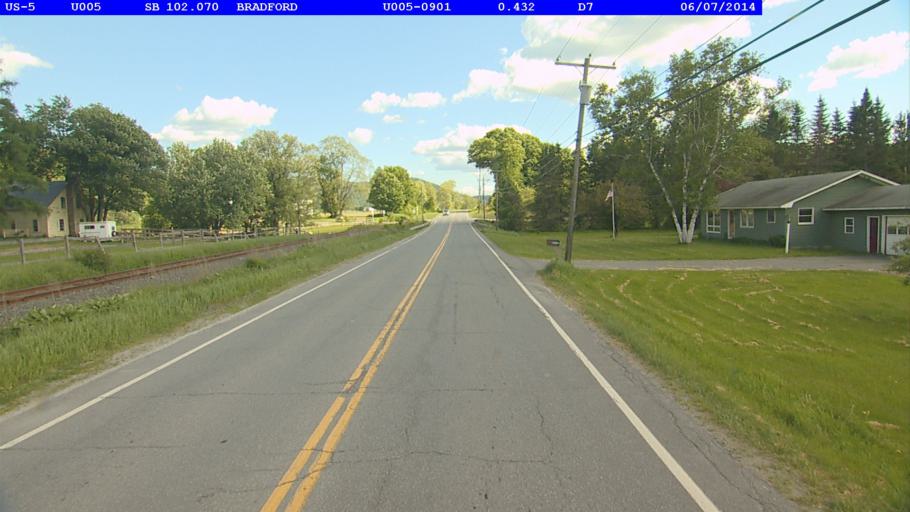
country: US
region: New Hampshire
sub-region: Grafton County
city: Orford
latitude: 43.9677
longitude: -72.1152
